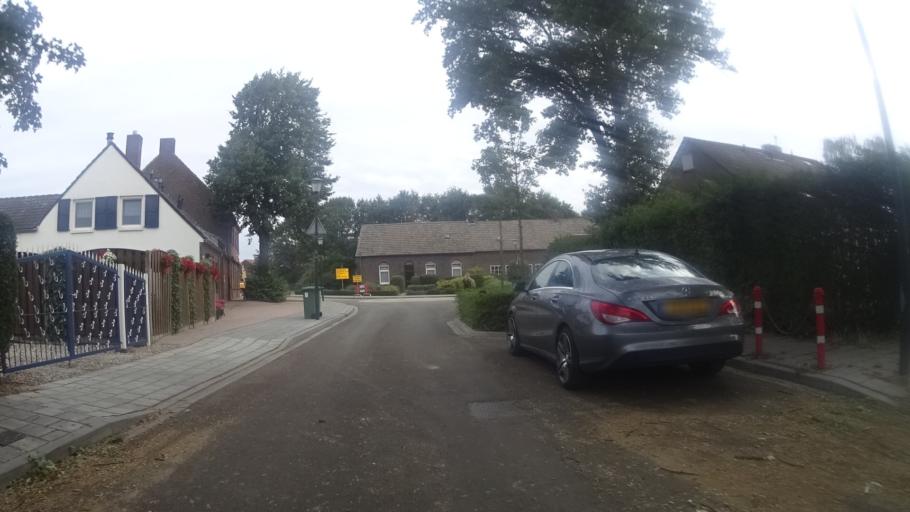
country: NL
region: Limburg
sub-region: Gemeente Venlo
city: Arcen
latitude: 51.4483
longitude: 6.1691
